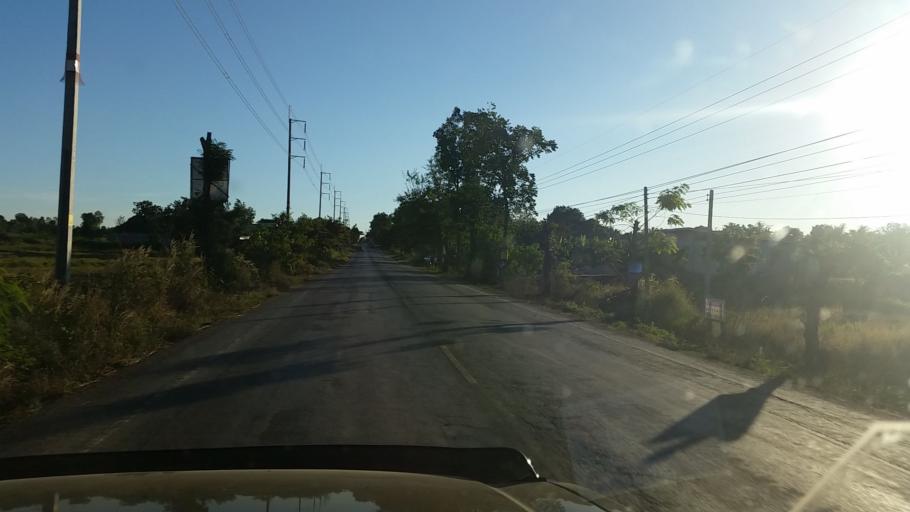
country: TH
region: Chaiyaphum
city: Nong Bua Rawe
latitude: 15.7254
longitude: 101.7449
